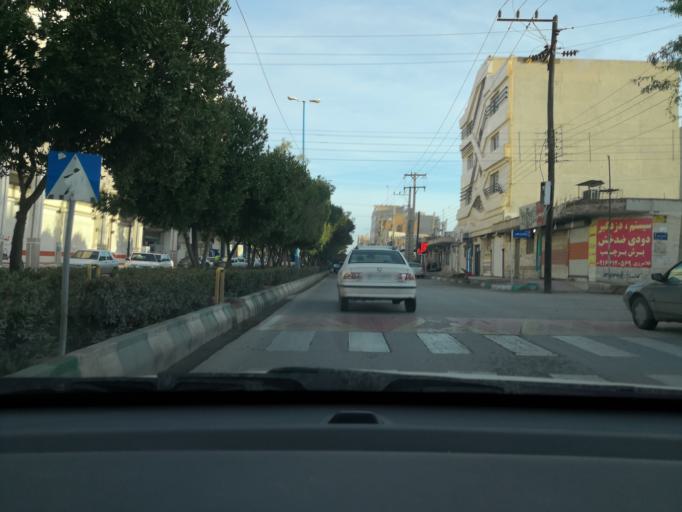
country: IR
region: Khuzestan
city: Ahvaz
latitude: 31.3521
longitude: 48.6772
